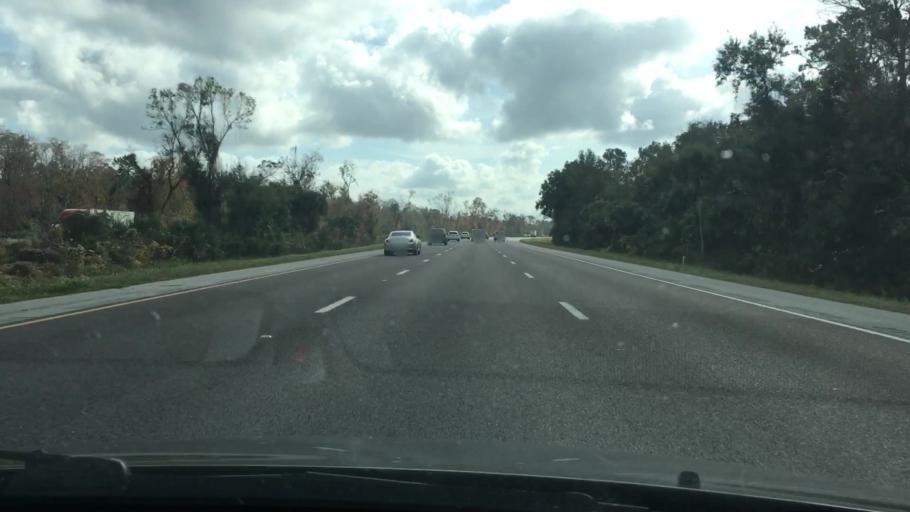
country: US
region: Florida
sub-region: Volusia County
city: Edgewater
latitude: 28.9276
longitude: -80.9402
